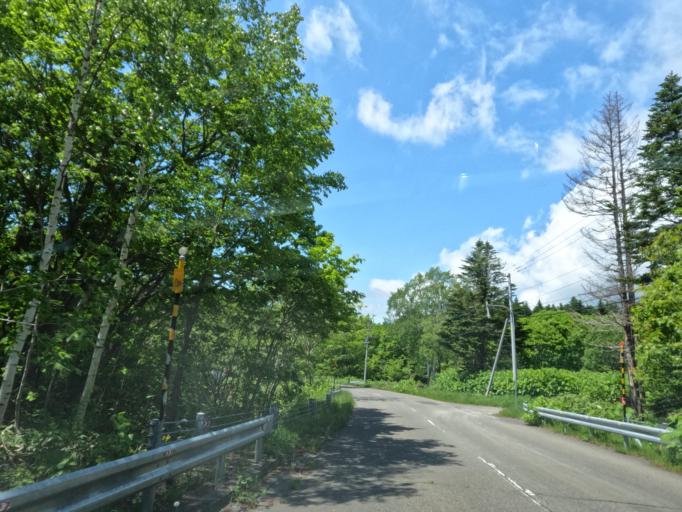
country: JP
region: Hokkaido
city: Tobetsu
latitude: 43.4166
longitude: 141.5867
